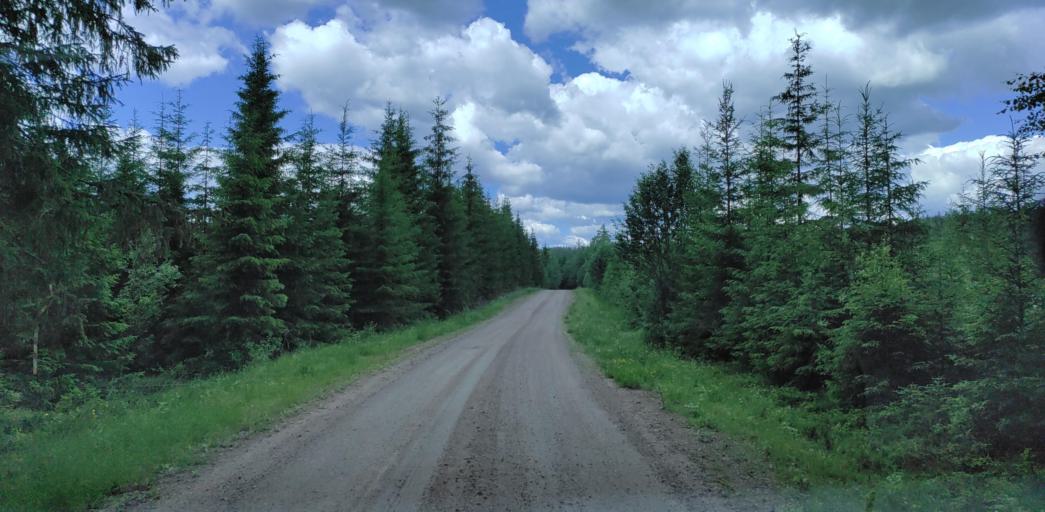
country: SE
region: Vaermland
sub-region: Hagfors Kommun
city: Ekshaerad
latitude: 60.0855
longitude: 13.4393
